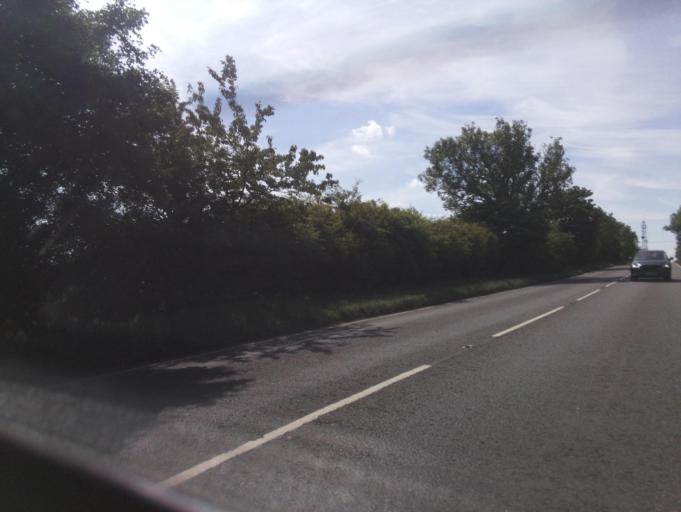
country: GB
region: England
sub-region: North Lincolnshire
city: Redbourne
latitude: 53.3889
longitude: -0.5473
